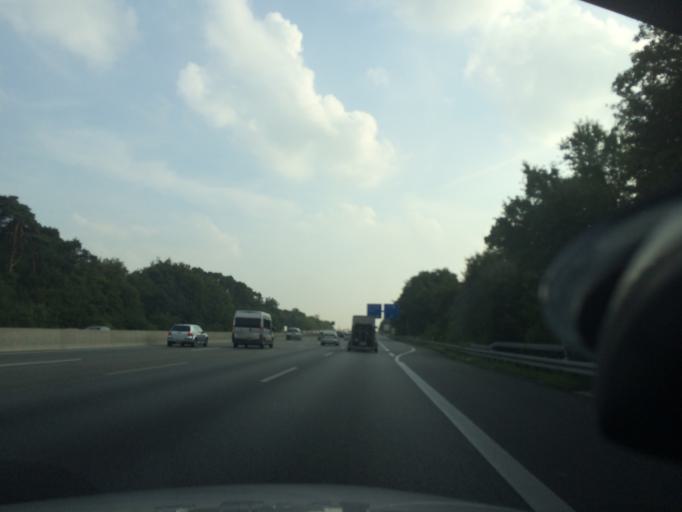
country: DE
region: Hesse
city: Weiterstadt
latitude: 49.9107
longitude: 8.6082
